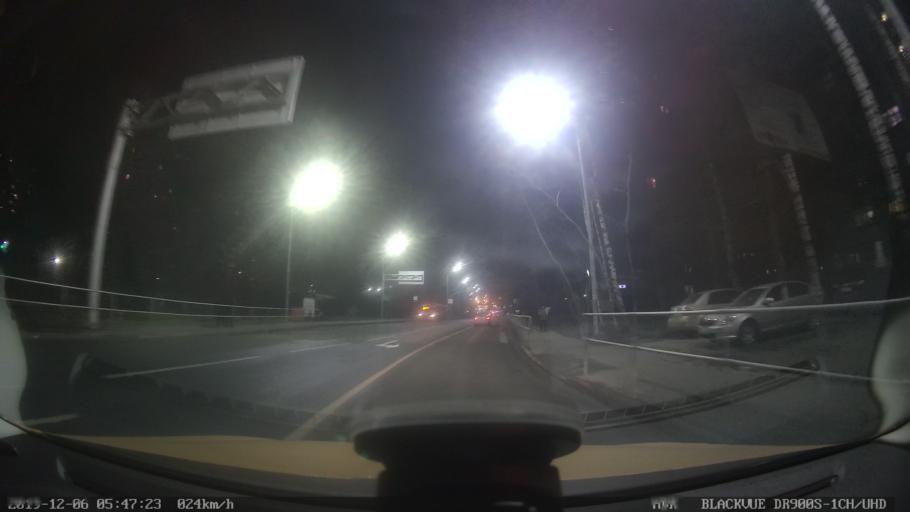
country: RU
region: Moscow
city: Vatutino
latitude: 55.8830
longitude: 37.6619
